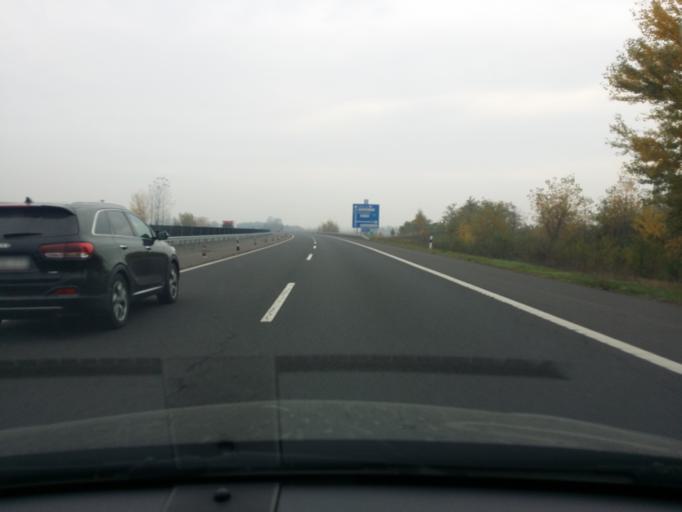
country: HU
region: Szabolcs-Szatmar-Bereg
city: Kalmanhaza
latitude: 47.8952
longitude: 21.6173
